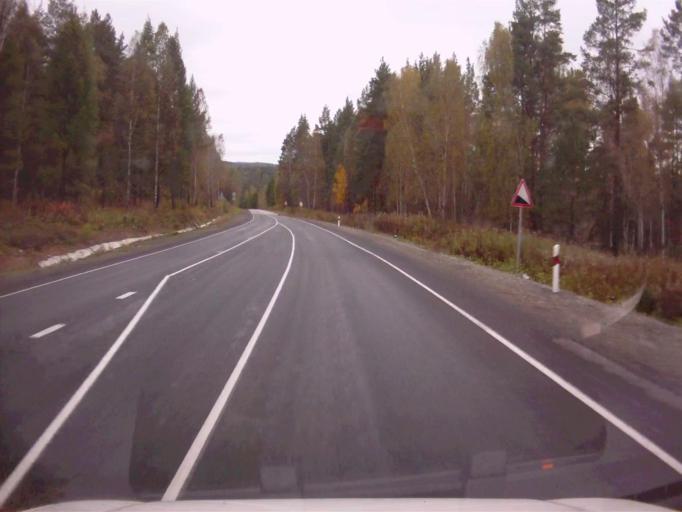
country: RU
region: Chelyabinsk
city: Nyazepetrovsk
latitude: 56.0620
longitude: 59.7282
